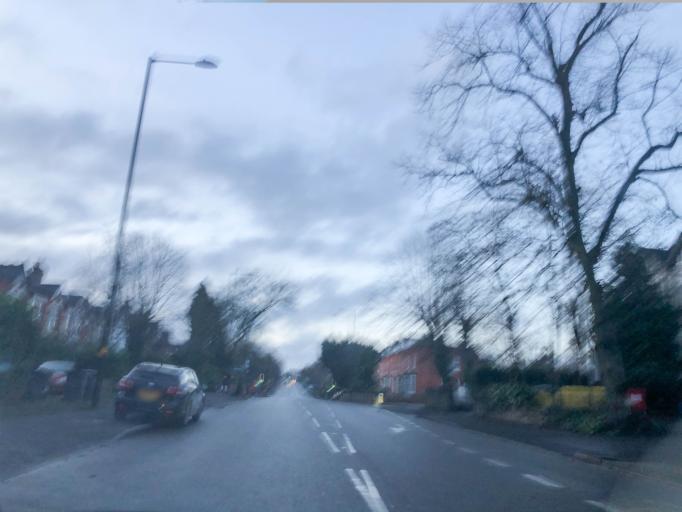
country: GB
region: England
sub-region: City and Borough of Birmingham
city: Birmingham
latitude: 52.4267
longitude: -1.8925
